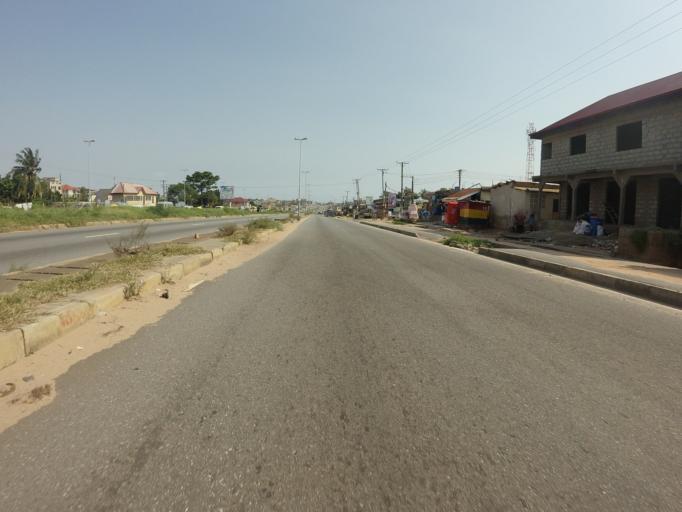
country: GH
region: Greater Accra
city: Gbawe
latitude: 5.6068
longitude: -0.2962
